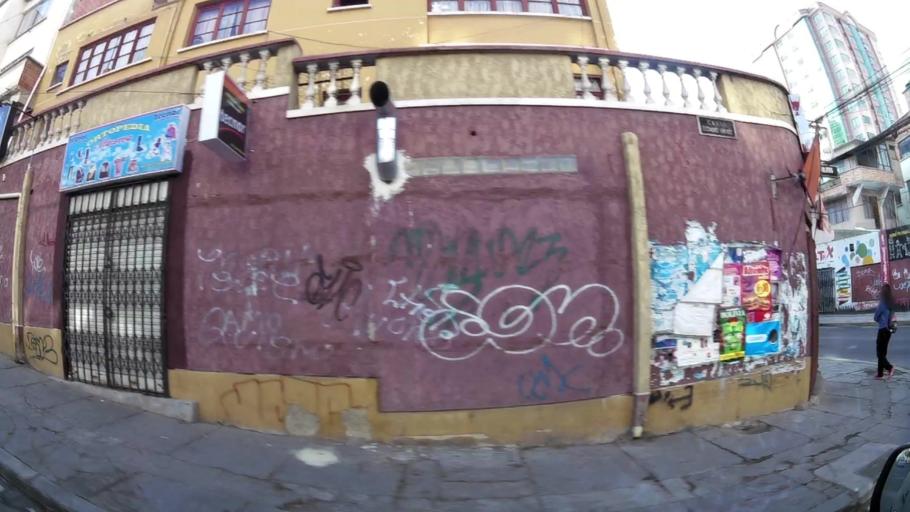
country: BO
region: La Paz
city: La Paz
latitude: -16.4970
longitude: -68.1219
